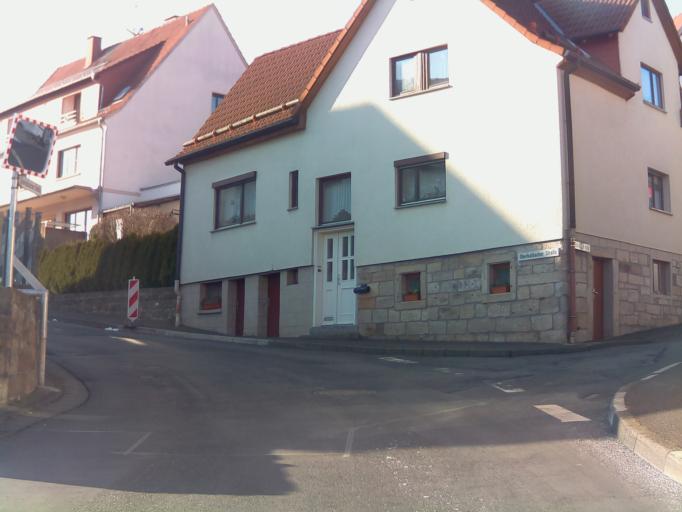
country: DE
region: Bavaria
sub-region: Regierungsbezirk Unterfranken
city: Motten
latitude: 50.4129
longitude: 9.7290
